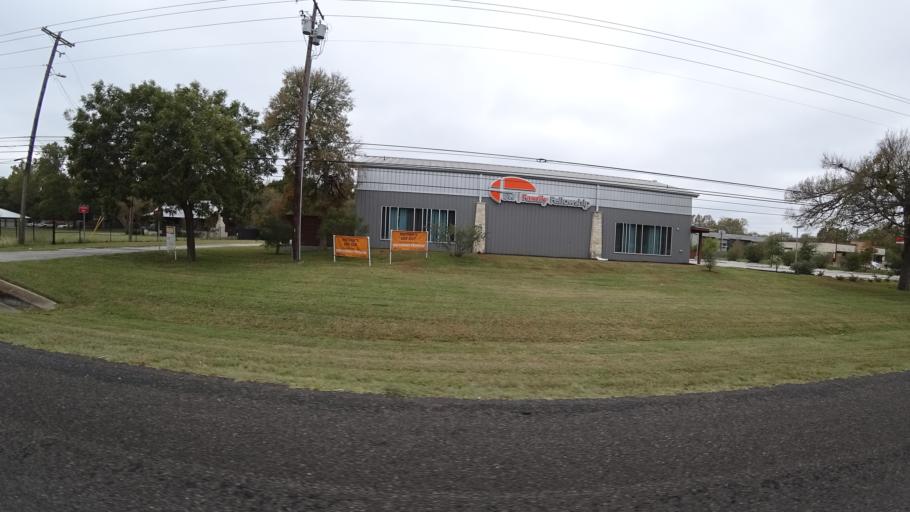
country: US
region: Texas
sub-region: Travis County
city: Barton Creek
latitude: 30.2463
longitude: -97.8870
